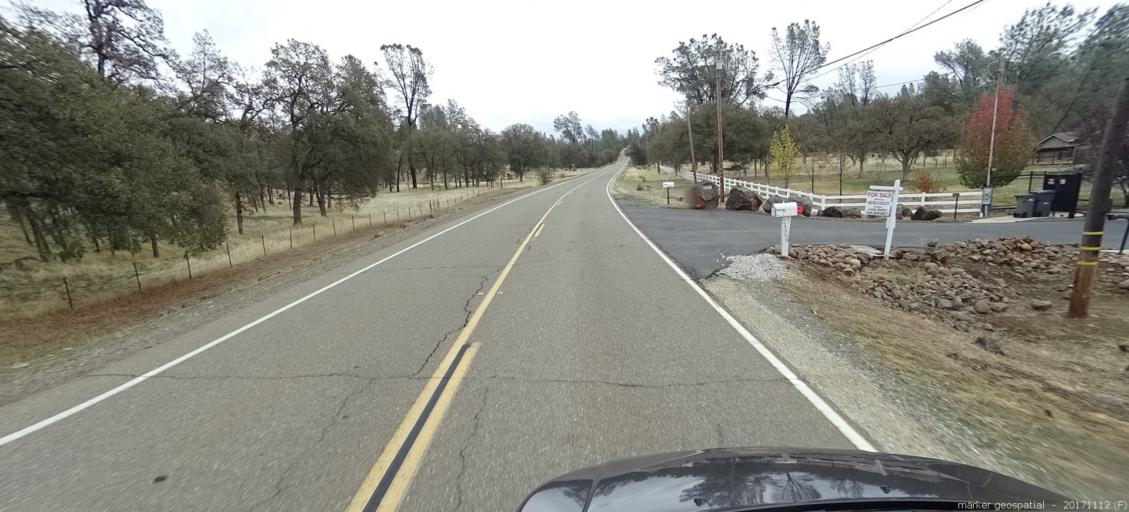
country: US
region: California
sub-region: Shasta County
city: Palo Cedro
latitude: 40.4877
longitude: -122.1388
